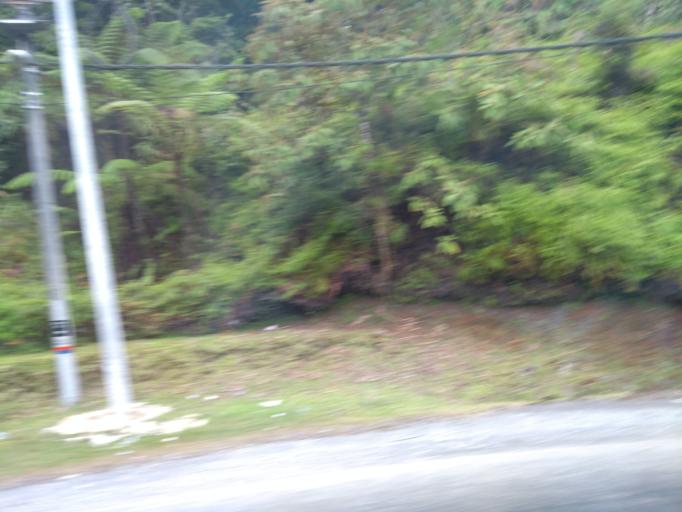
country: MY
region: Pahang
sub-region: Cameron Highlands
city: Tanah Rata
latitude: 4.5080
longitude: 101.4136
